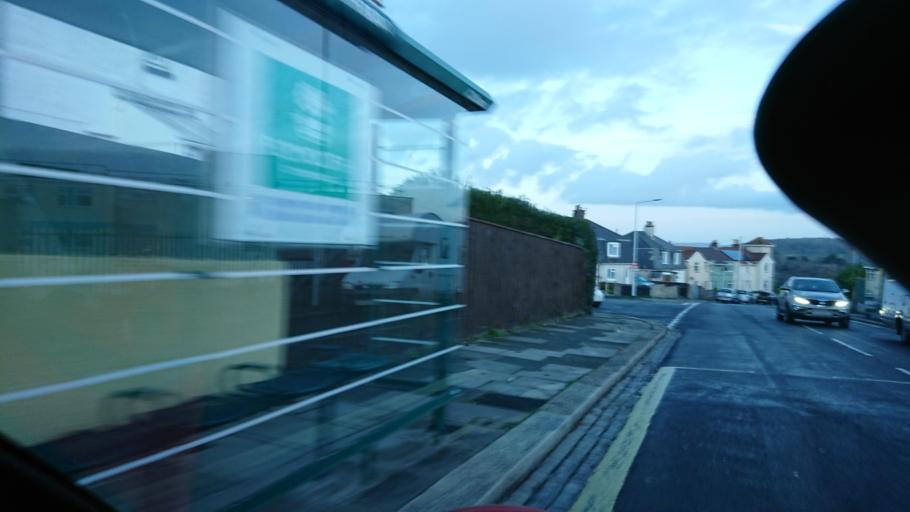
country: GB
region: England
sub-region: Plymouth
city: Plymstock
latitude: 50.3793
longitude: -4.1109
